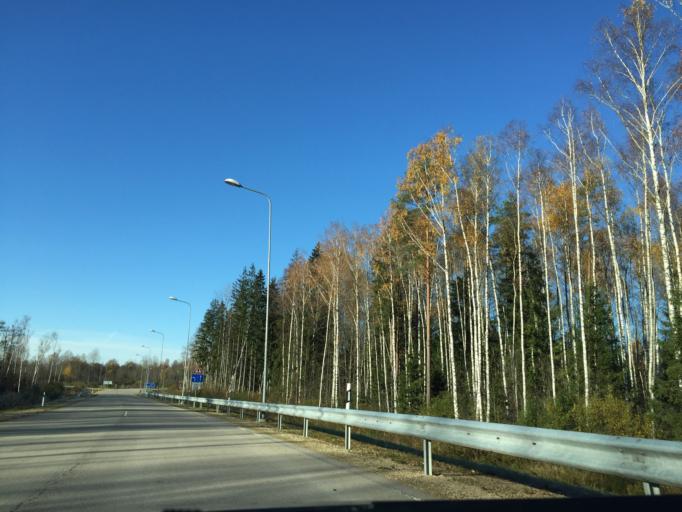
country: LV
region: Aizkraukles Rajons
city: Aizkraukle
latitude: 56.7045
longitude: 25.2807
